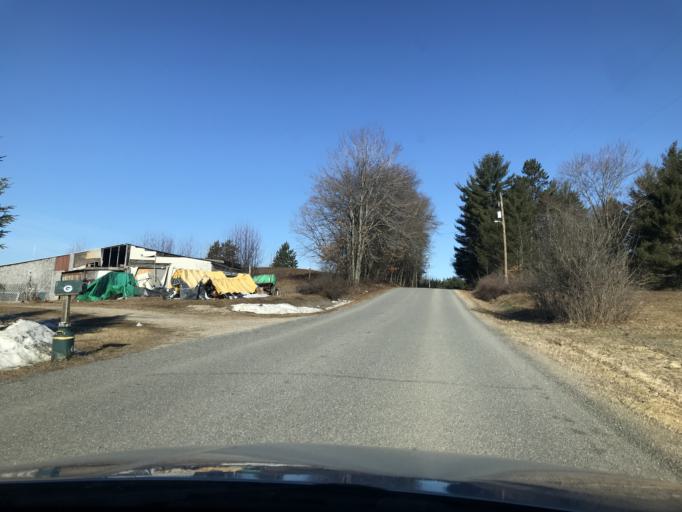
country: US
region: Wisconsin
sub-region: Marinette County
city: Niagara
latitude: 45.3887
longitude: -88.0477
